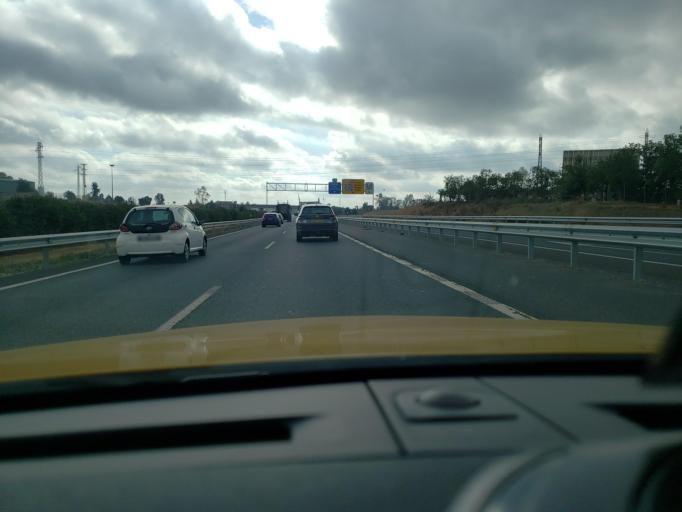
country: ES
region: Andalusia
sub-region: Provincia de Sevilla
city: Gelves
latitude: 37.3048
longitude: -5.9824
